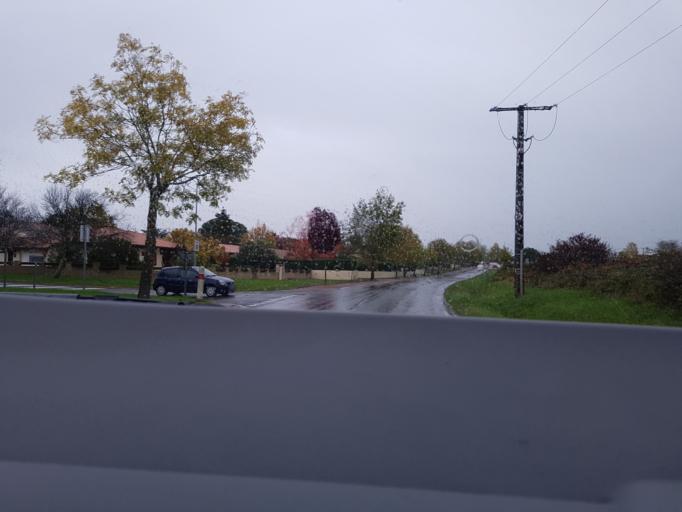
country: FR
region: Aquitaine
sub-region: Departement de la Gironde
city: Cubzac-les-Ponts
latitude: 44.9898
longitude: -0.4455
